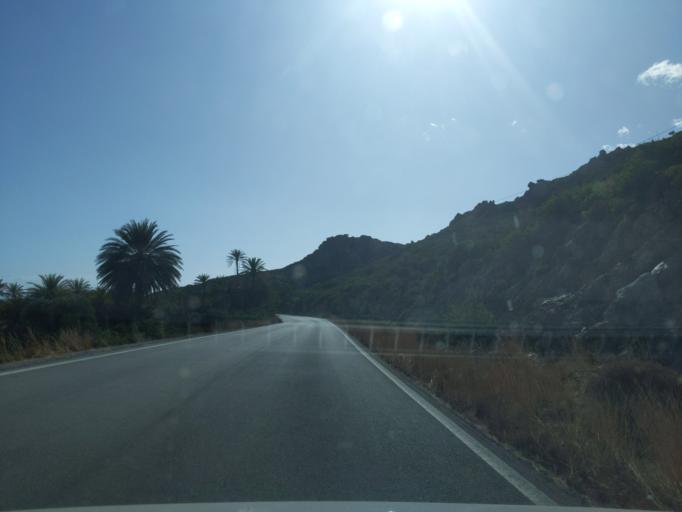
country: GR
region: Crete
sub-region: Nomos Lasithiou
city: Palekastro
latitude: 35.2546
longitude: 26.2600
